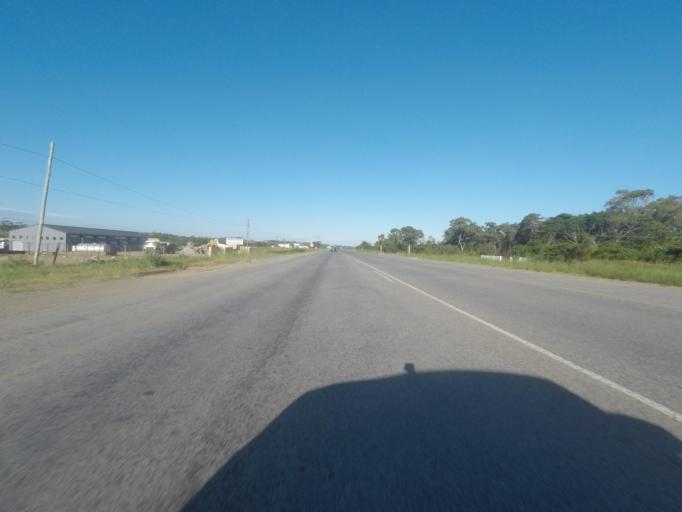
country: ZA
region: Eastern Cape
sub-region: Buffalo City Metropolitan Municipality
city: East London
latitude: -33.0558
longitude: 27.8007
